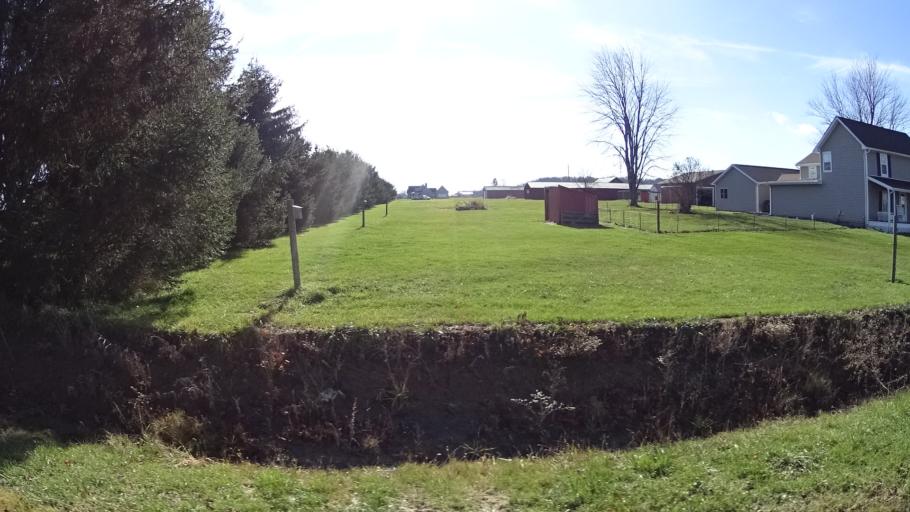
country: US
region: Ohio
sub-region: Lorain County
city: Wellington
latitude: 41.0844
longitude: -82.1824
